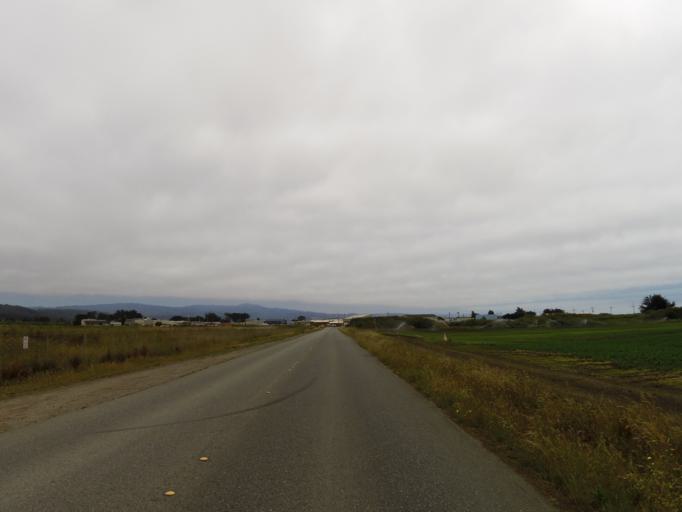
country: US
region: California
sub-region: San Mateo County
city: Moss Beach
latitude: 37.5078
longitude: -122.4962
